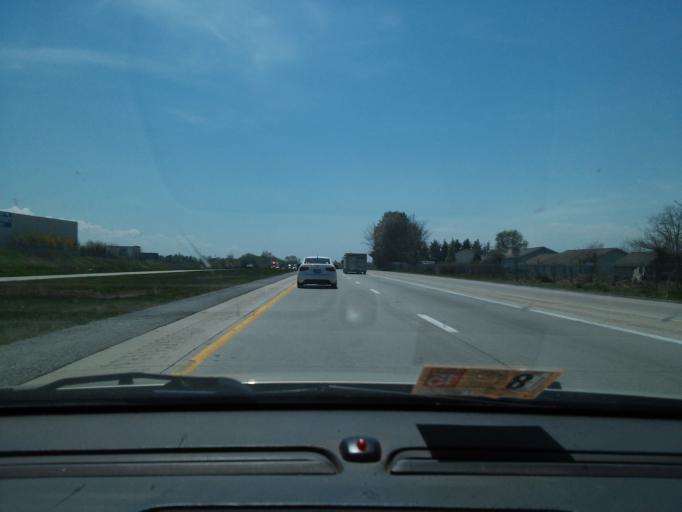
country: US
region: Pennsylvania
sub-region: Franklin County
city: Scotland
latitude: 39.9620
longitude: -77.5787
